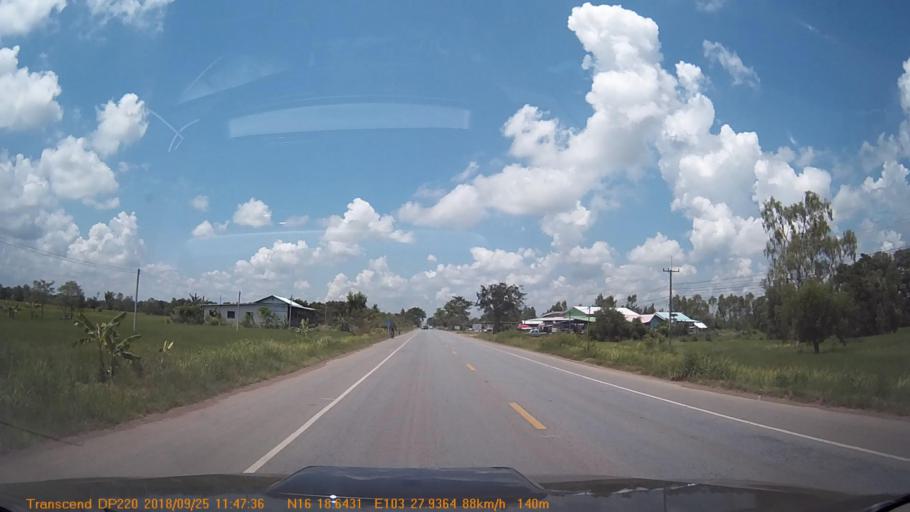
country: TH
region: Kalasin
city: Khong Chai
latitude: 16.3108
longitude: 103.4655
